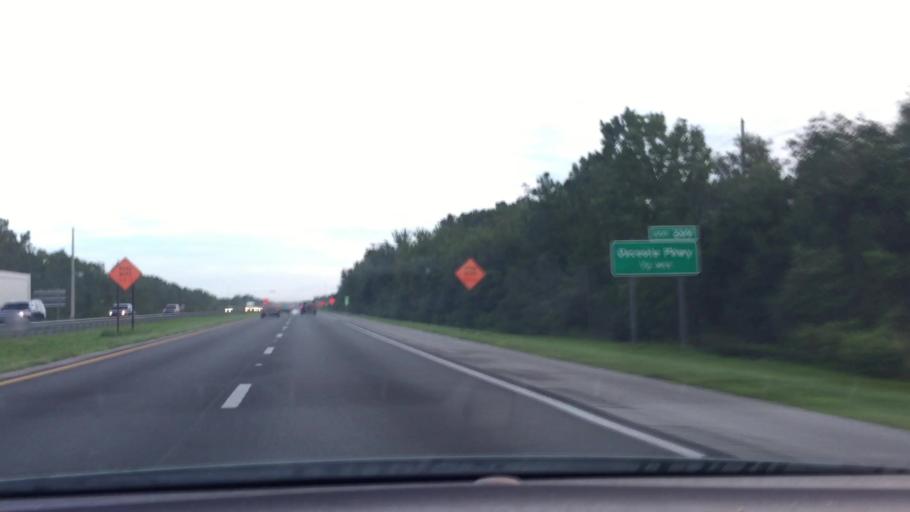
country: US
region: Florida
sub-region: Osceola County
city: Buenaventura Lakes
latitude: 28.3299
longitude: -81.3766
